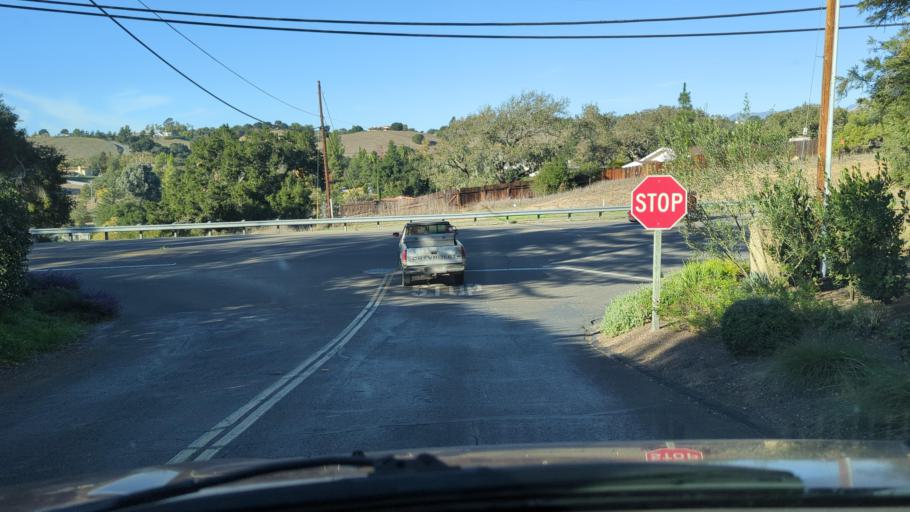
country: US
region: California
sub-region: Santa Barbara County
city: Solvang
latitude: 34.6058
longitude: -120.1111
